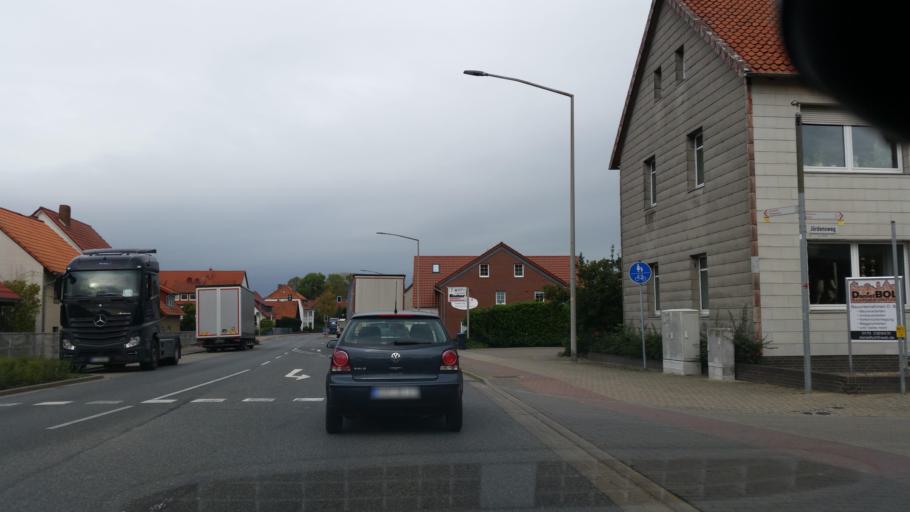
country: DE
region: Lower Saxony
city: Giesen
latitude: 52.1928
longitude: 9.9221
